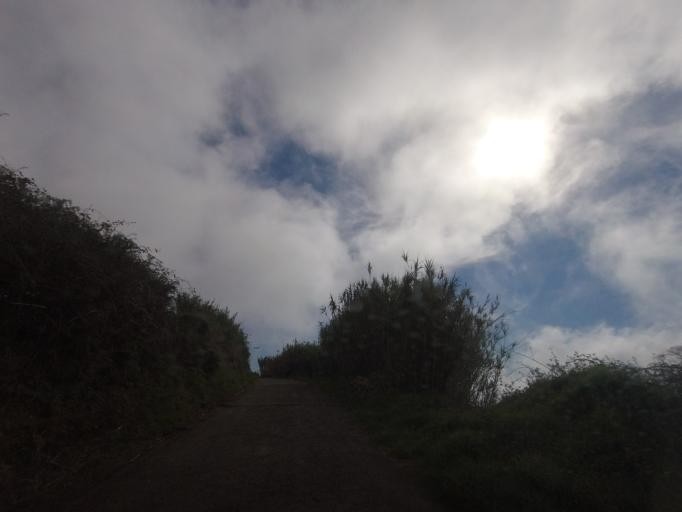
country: PT
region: Madeira
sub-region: Calheta
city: Faja da Ovelha
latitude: 32.7602
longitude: -17.2197
